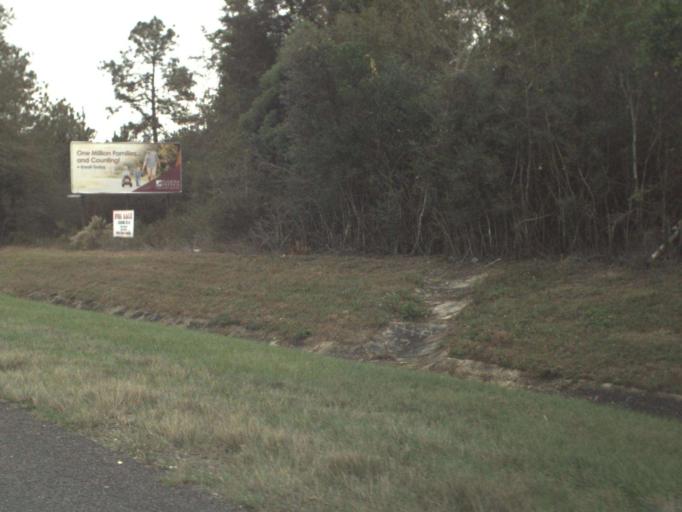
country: US
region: Florida
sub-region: Escambia County
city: Cantonment
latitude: 30.6315
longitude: -87.3344
